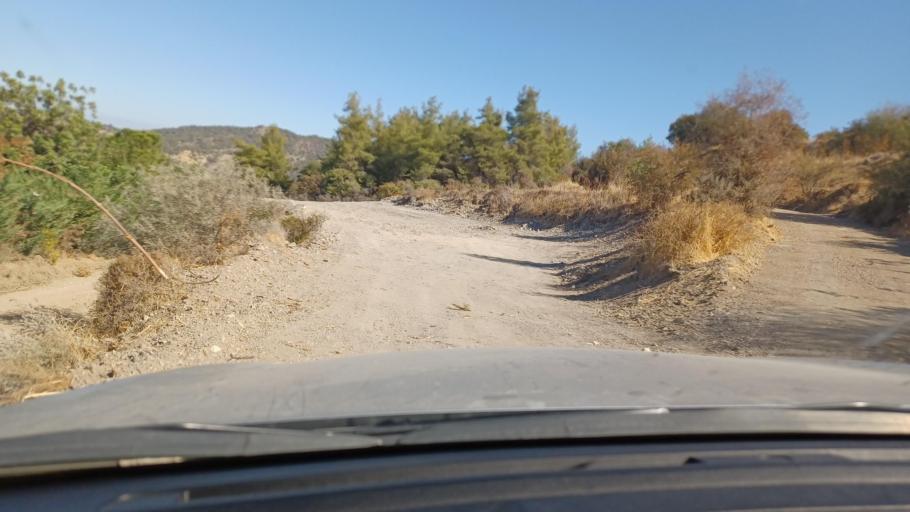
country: CY
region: Pafos
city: Polis
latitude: 35.0035
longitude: 32.5110
